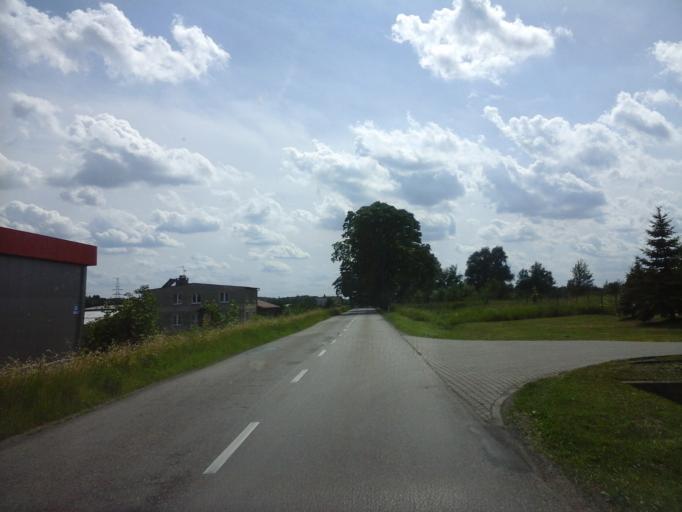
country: PL
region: West Pomeranian Voivodeship
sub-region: Powiat swidwinski
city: Swidwin
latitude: 53.7618
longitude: 15.7494
